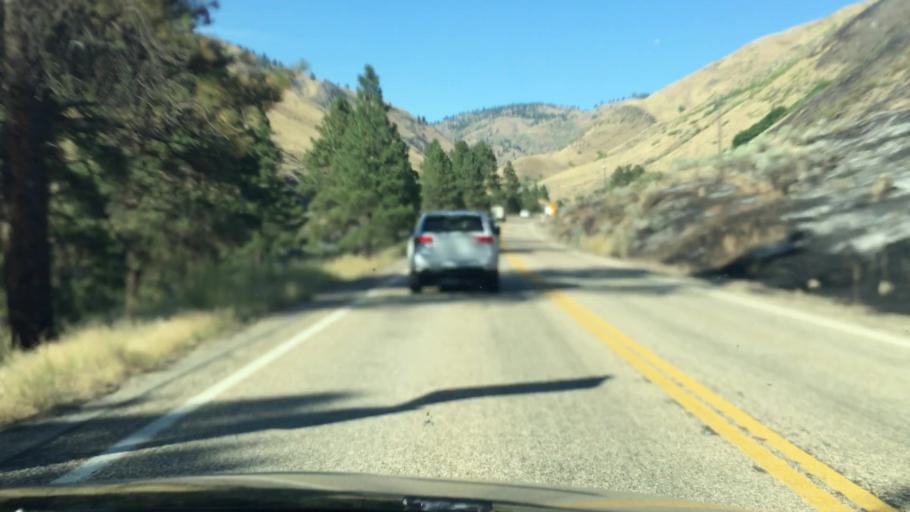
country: US
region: Idaho
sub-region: Gem County
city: Emmett
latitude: 44.0119
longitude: -116.1605
